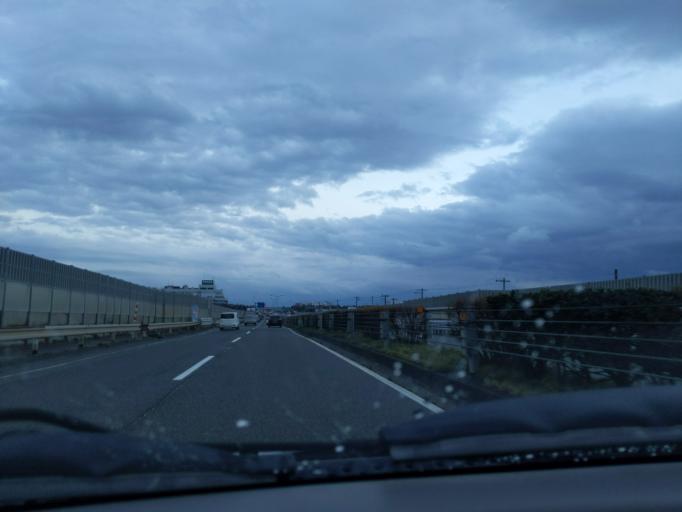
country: JP
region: Niigata
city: Kameda-honcho
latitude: 37.8881
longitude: 139.0768
